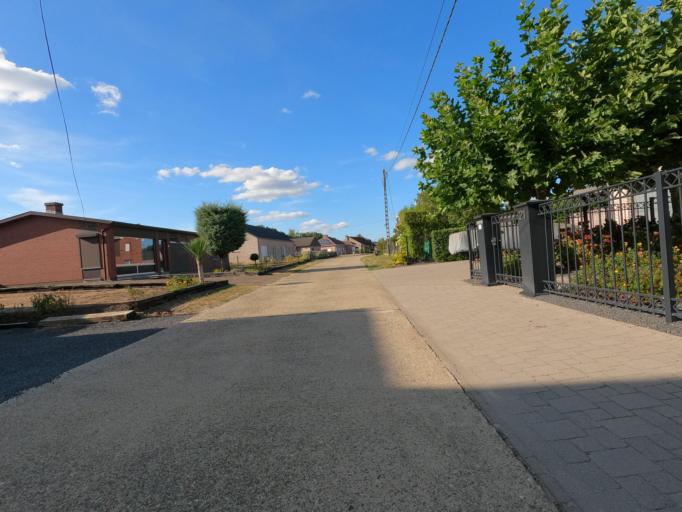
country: BE
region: Flanders
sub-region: Provincie Antwerpen
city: Hulshout
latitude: 51.0673
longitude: 4.8216
